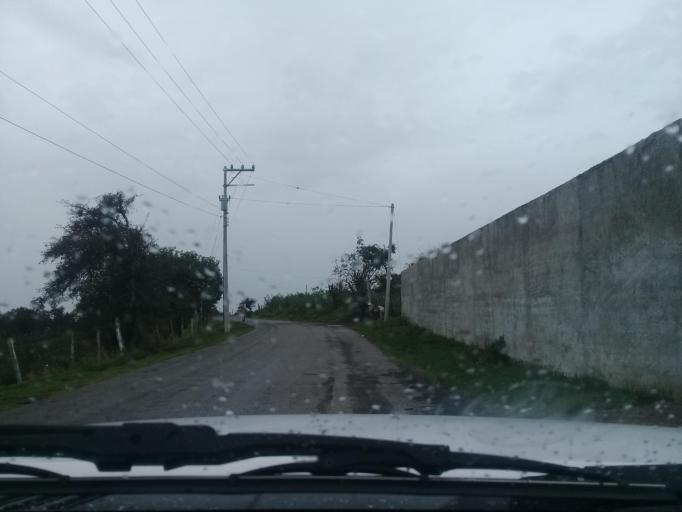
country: MX
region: Veracruz
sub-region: Acajete
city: La Joya
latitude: 19.6120
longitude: -97.0049
